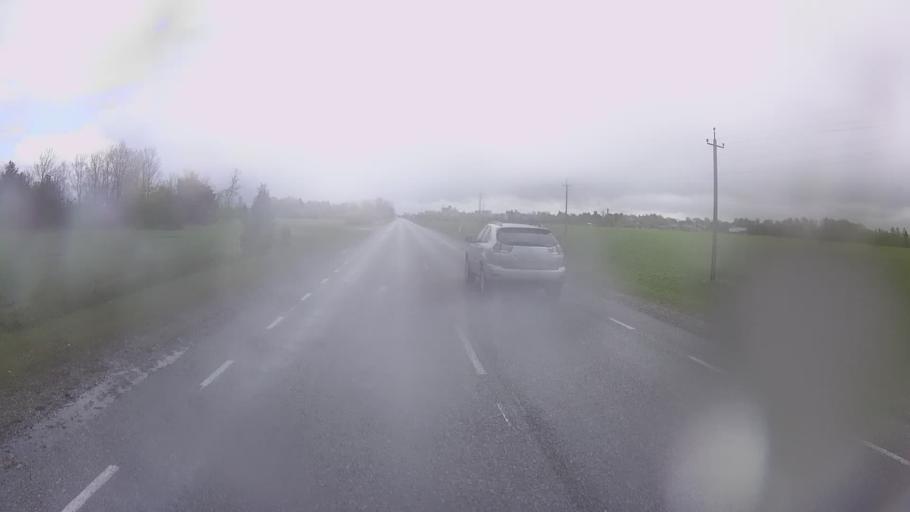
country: EE
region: Hiiumaa
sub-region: Kaerdla linn
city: Kardla
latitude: 58.8278
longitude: 22.7589
